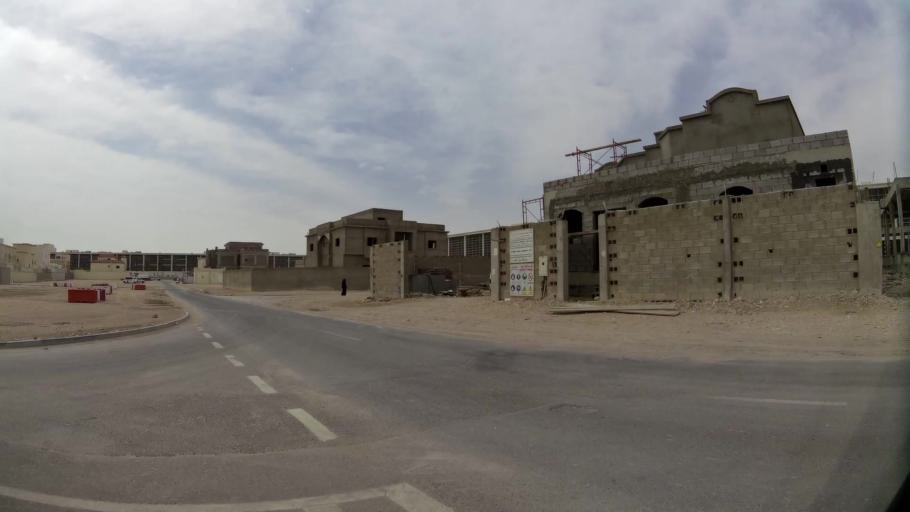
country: QA
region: Al Wakrah
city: Al Wukayr
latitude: 25.1968
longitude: 51.4546
